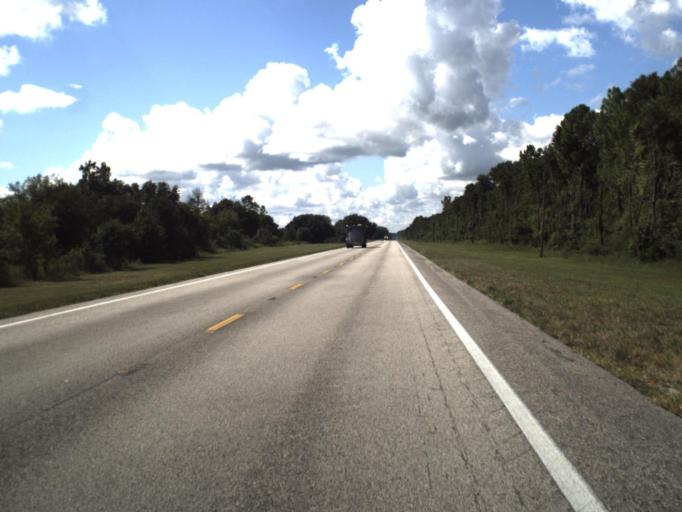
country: US
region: Florida
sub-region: Pasco County
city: Zephyrhills North
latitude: 28.2895
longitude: -82.0555
